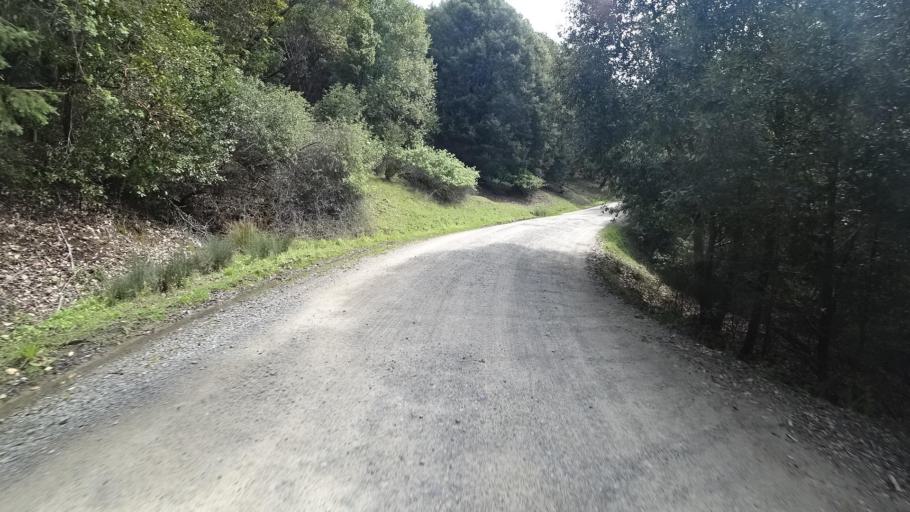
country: US
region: California
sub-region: Humboldt County
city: Redway
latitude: 40.0395
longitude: -123.8453
